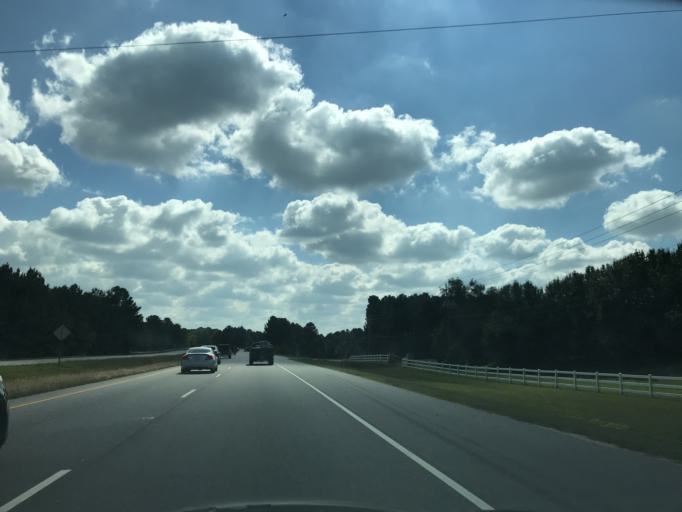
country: US
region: North Carolina
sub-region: Wake County
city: Wake Forest
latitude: 35.9291
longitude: -78.5434
